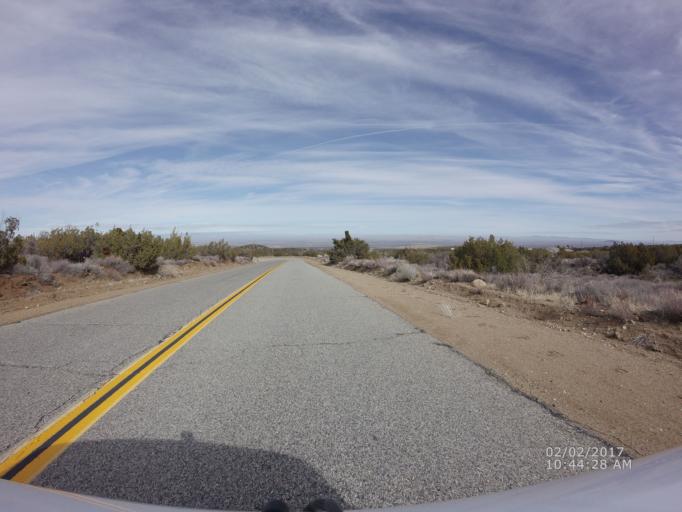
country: US
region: California
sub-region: Los Angeles County
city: Littlerock
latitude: 34.4470
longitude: -117.9476
